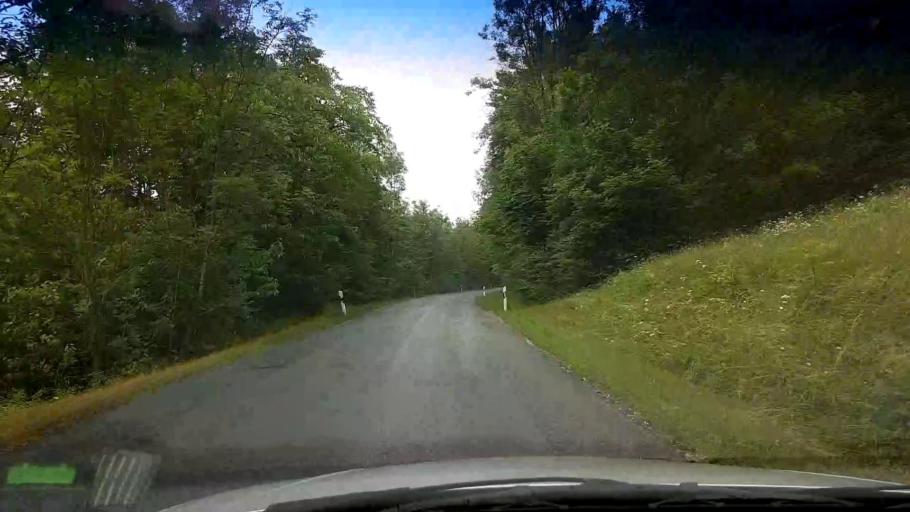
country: DE
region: Bavaria
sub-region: Upper Franconia
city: Wattendorf
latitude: 50.0652
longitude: 11.0795
